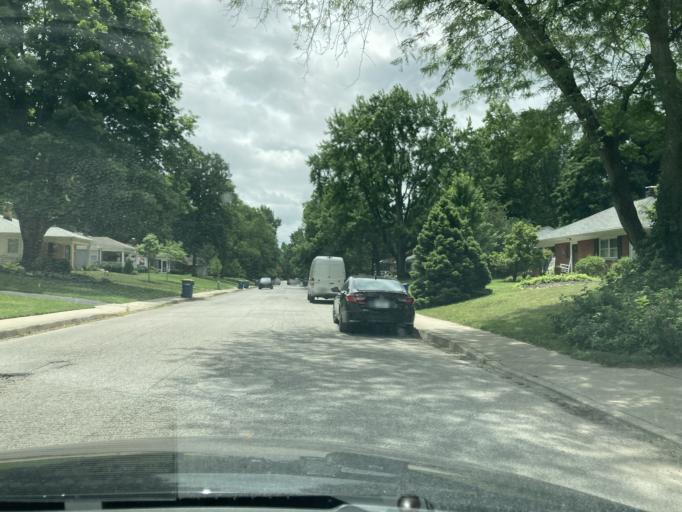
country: US
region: Indiana
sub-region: Marion County
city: Broad Ripple
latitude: 39.8565
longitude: -86.1329
